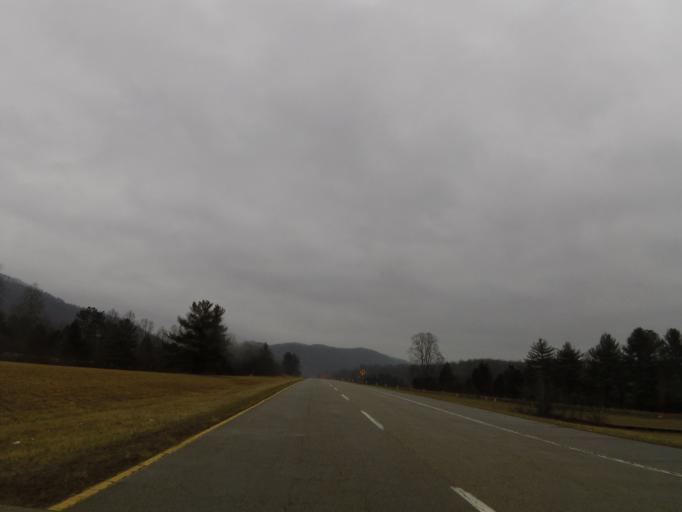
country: US
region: Tennessee
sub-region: Roane County
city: Harriman
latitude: 35.9709
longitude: -84.4978
